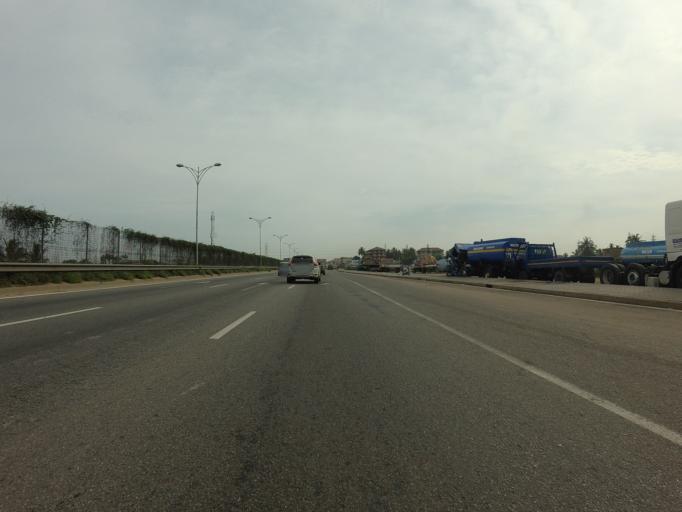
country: GH
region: Greater Accra
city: Gbawe
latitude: 5.5807
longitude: -0.2771
